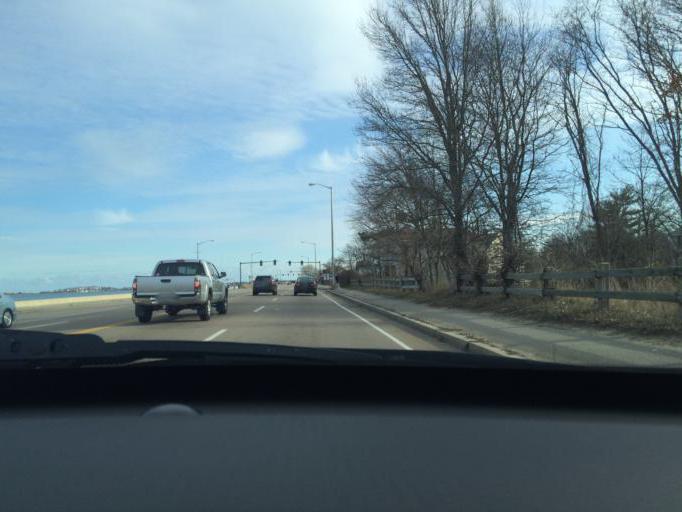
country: US
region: Massachusetts
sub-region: Norfolk County
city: Quincy
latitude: 42.2761
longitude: -71.0079
